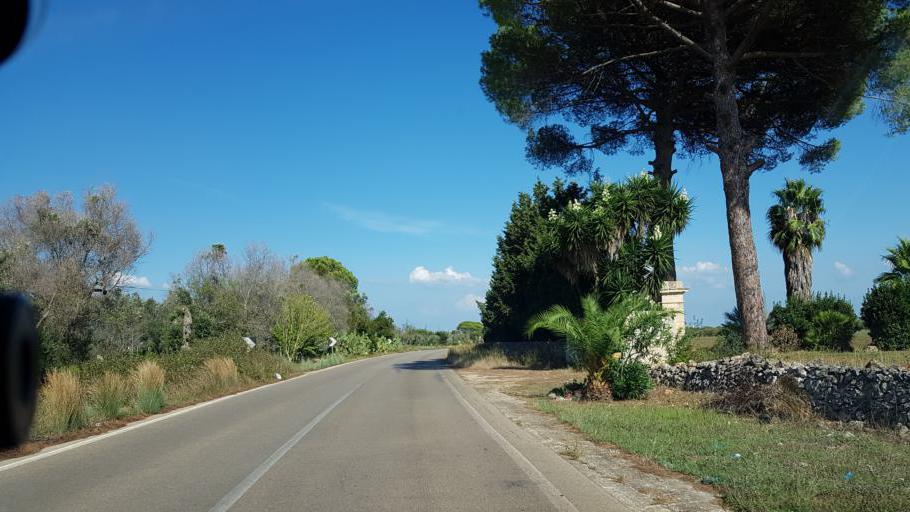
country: IT
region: Apulia
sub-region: Provincia di Lecce
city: Monteroni di Lecce
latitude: 40.2970
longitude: 18.0997
